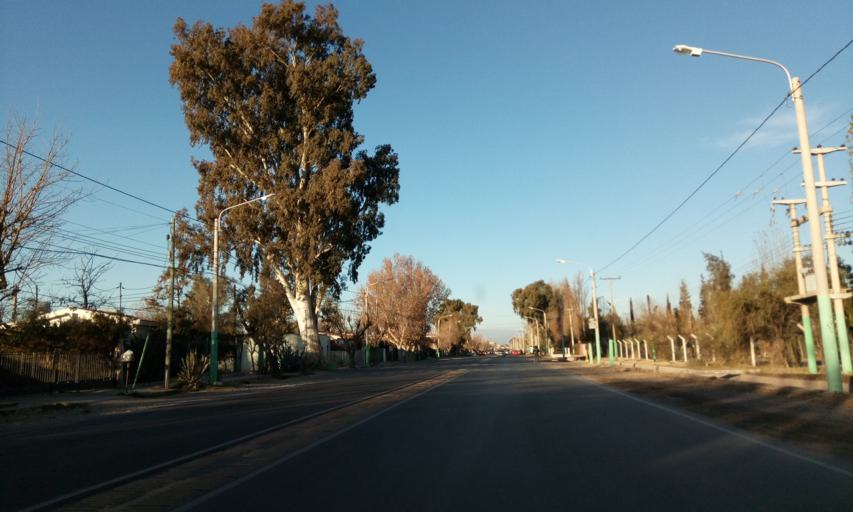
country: AR
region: San Juan
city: San Juan
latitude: -31.5388
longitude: -68.5894
